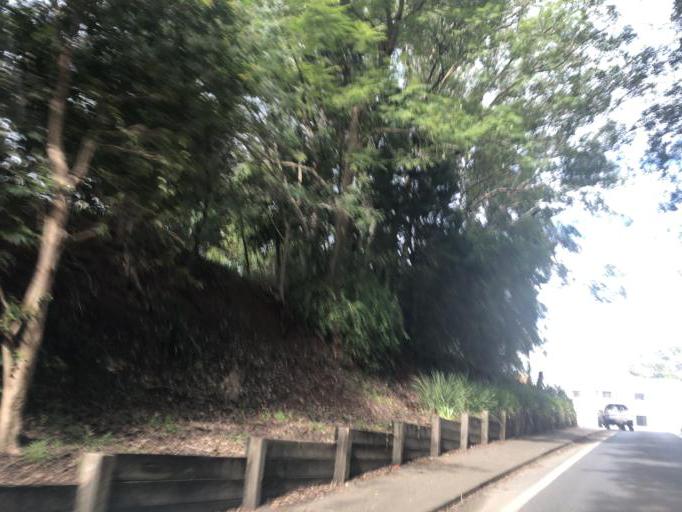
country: AU
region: New South Wales
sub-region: Bellingen
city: Bellingen
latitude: -30.4516
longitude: 152.8983
